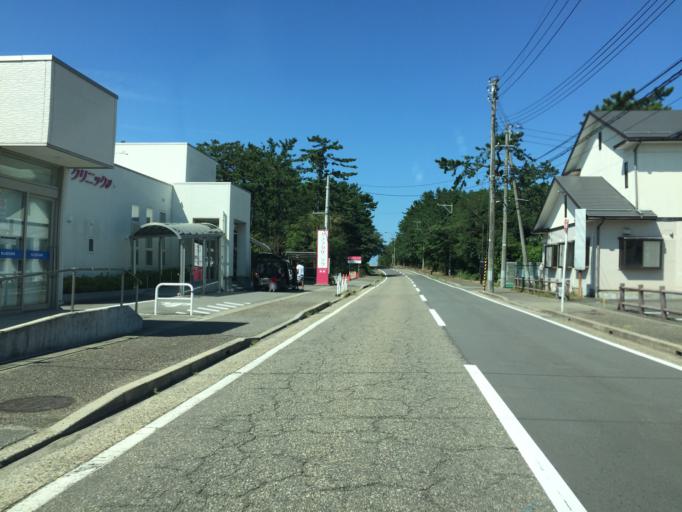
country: JP
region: Niigata
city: Niigata-shi
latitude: 37.8995
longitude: 138.9940
